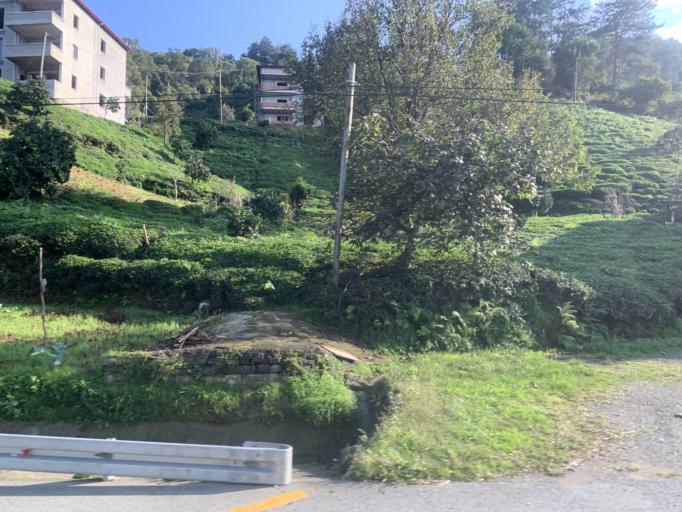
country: TR
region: Trabzon
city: Of
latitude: 40.9324
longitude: 40.2405
